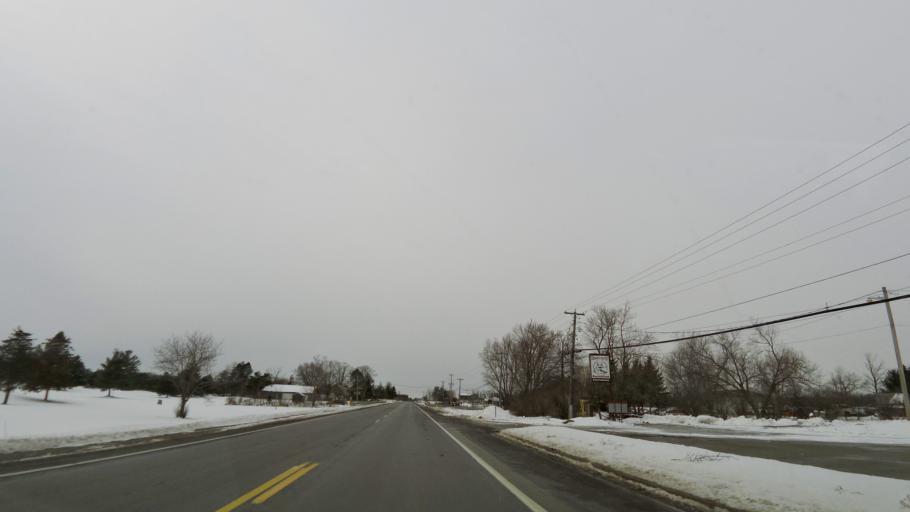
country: CA
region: Ontario
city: Cambridge
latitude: 43.3167
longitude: -80.1749
